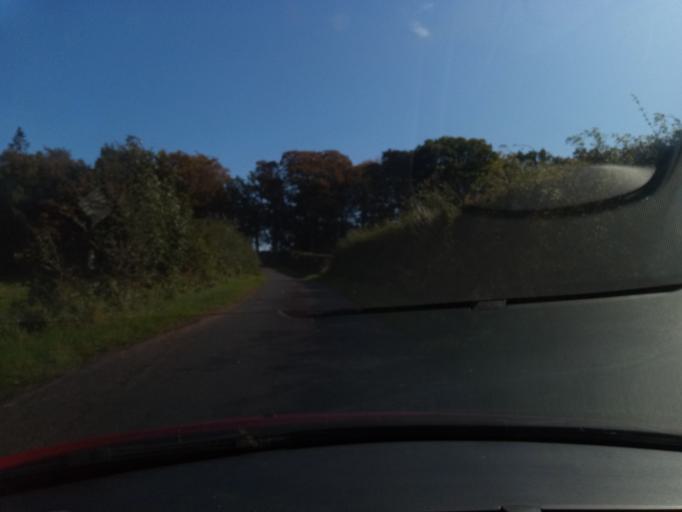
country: GB
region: Scotland
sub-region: The Scottish Borders
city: Jedburgh
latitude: 55.5109
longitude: -2.4824
